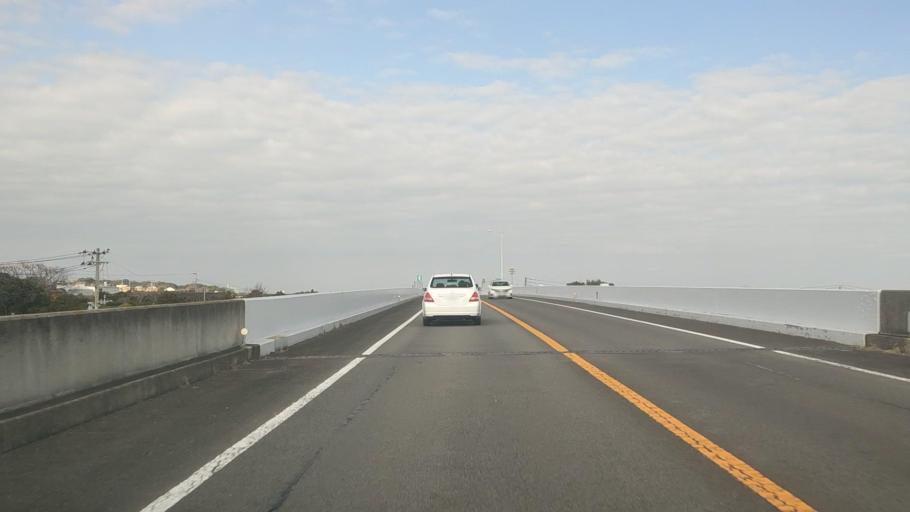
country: JP
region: Nagasaki
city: Shimabara
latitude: 32.7388
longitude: 130.3711
